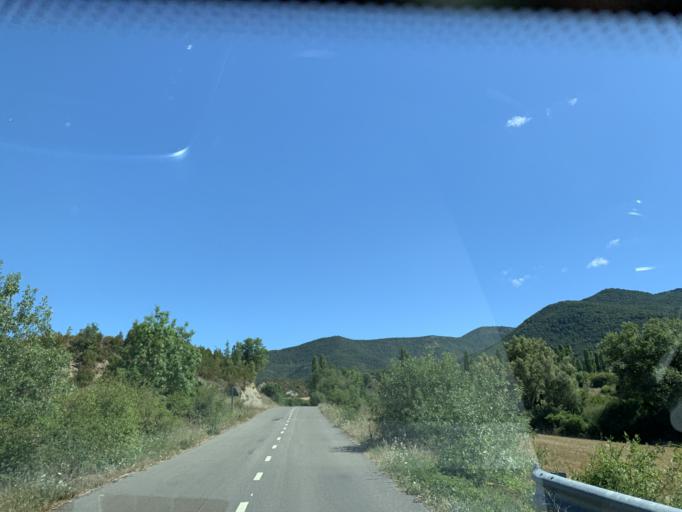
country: ES
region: Aragon
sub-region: Provincia de Huesca
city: Sabinanigo
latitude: 42.5354
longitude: -0.3219
